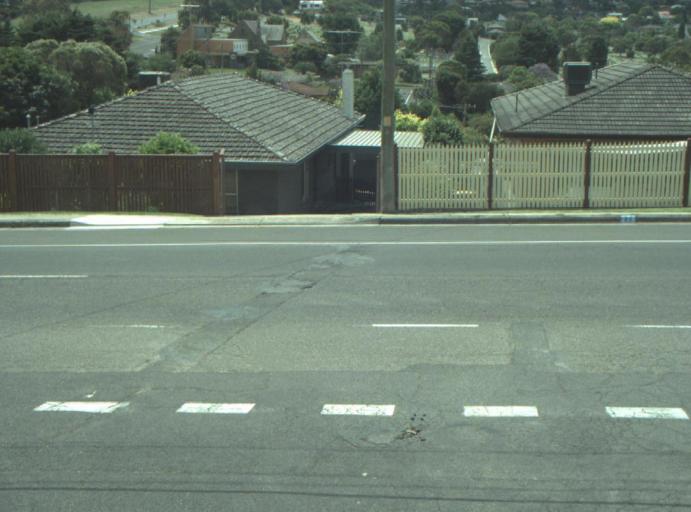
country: AU
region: Victoria
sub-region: Greater Geelong
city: Wandana Heights
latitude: -38.1717
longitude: 144.3106
